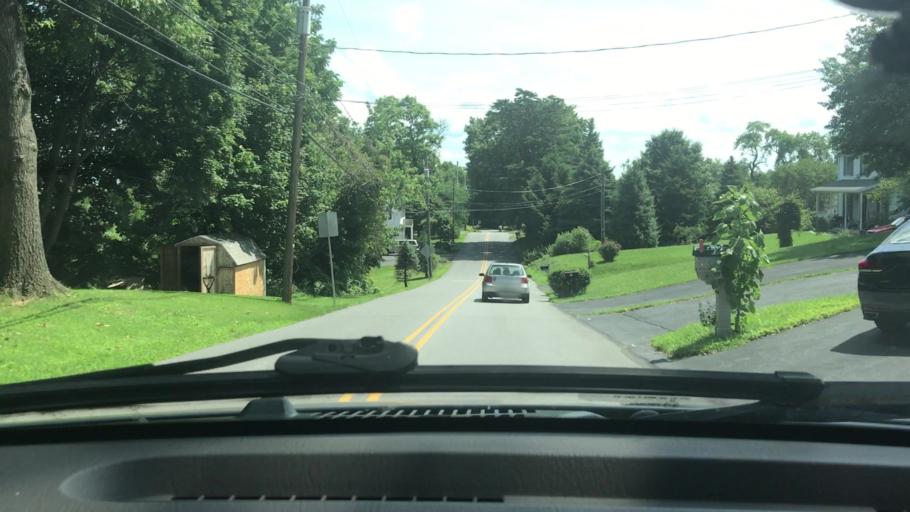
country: US
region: Pennsylvania
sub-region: Dauphin County
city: Rutherford
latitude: 40.2583
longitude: -76.7477
